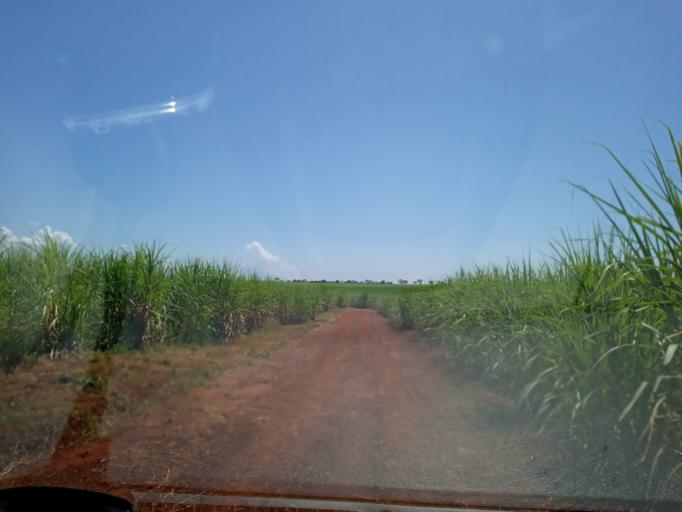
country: BR
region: Goias
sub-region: Itumbiara
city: Itumbiara
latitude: -18.4331
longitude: -49.1515
